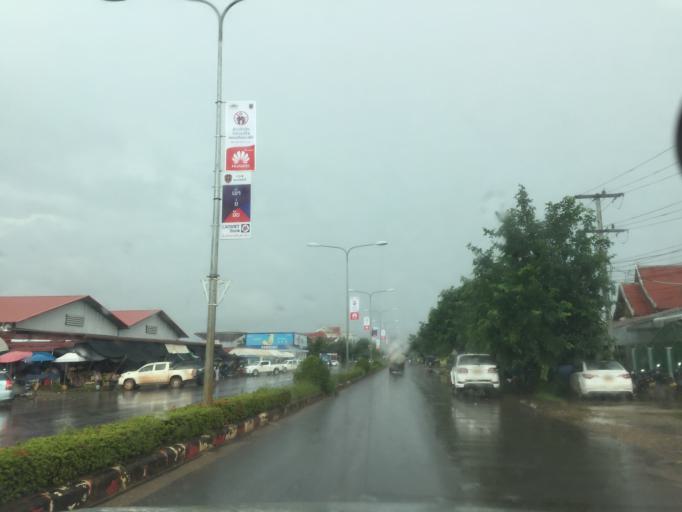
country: LA
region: Attapu
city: Attapu
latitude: 14.8168
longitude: 106.8181
